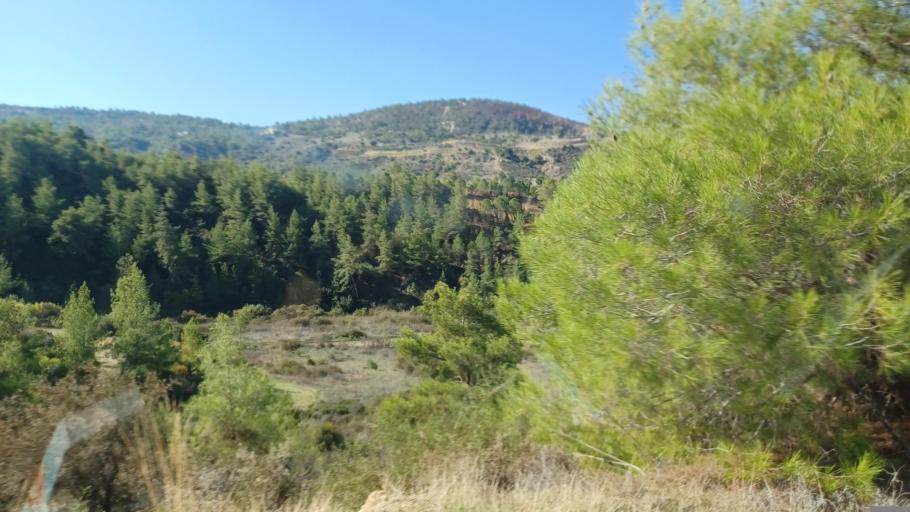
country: CY
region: Pafos
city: Polis
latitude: 35.0284
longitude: 32.4937
